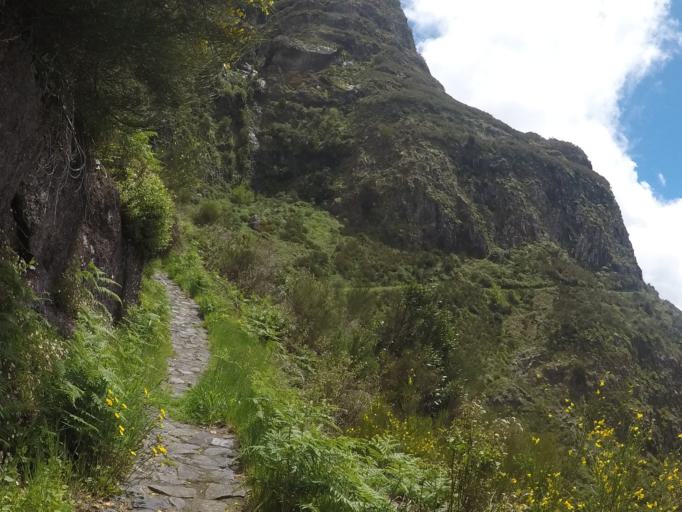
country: PT
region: Madeira
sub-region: Camara de Lobos
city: Curral das Freiras
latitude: 32.7402
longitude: -17.0021
